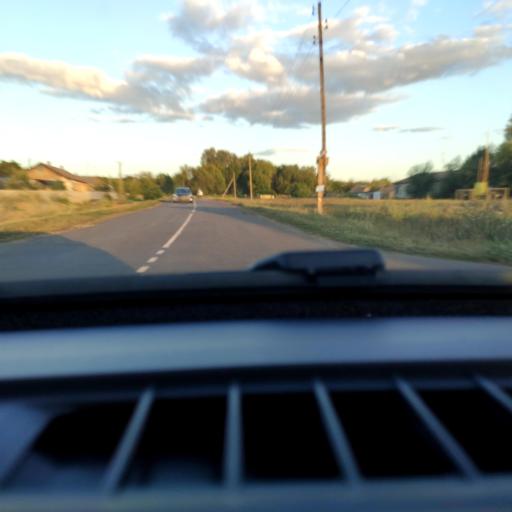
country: RU
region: Voronezj
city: Orlovo
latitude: 51.6139
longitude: 39.8082
